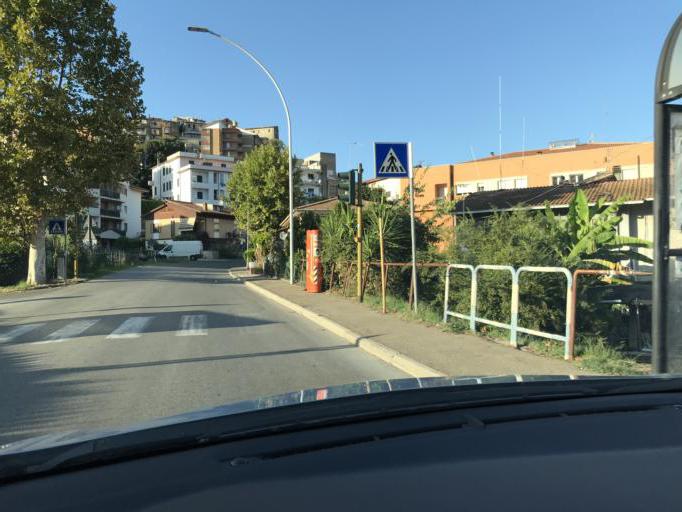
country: IT
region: Latium
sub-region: Provincia di Viterbo
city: Orte
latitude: 42.4569
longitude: 12.3871
